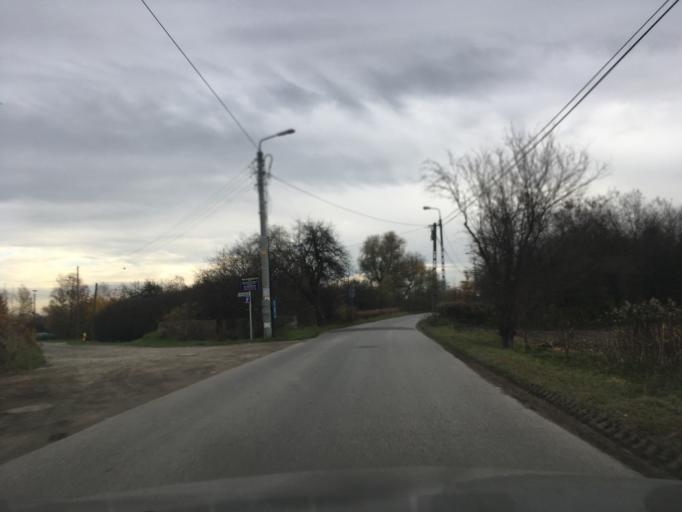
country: PL
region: Masovian Voivodeship
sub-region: Powiat piaseczynski
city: Piaseczno
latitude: 52.0477
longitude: 20.9759
